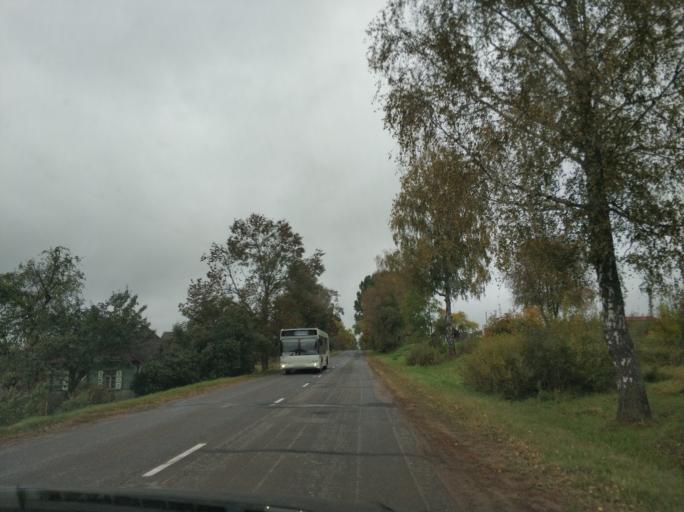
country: BY
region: Vitebsk
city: Polatsk
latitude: 55.4295
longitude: 29.0012
